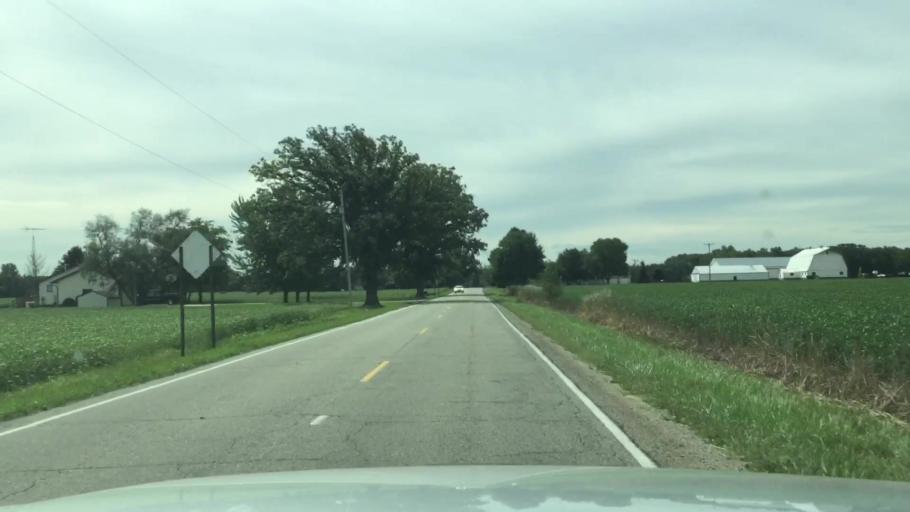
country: US
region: Michigan
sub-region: Genesee County
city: Montrose
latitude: 43.1154
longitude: -83.9880
